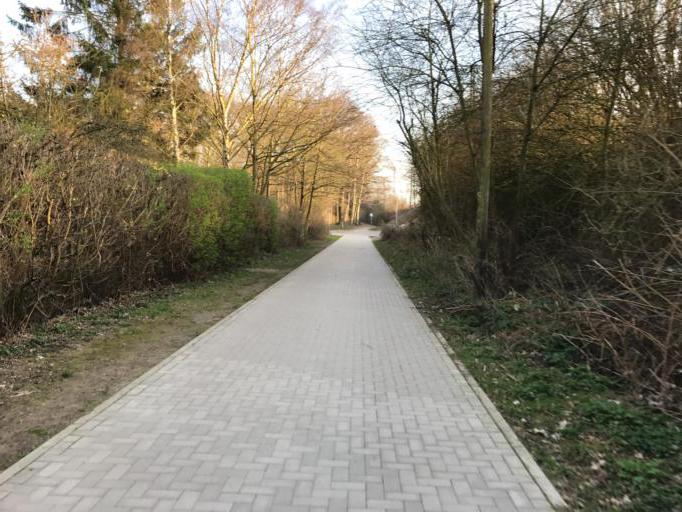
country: DE
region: Lower Saxony
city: Hannover
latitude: 52.3548
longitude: 9.7711
